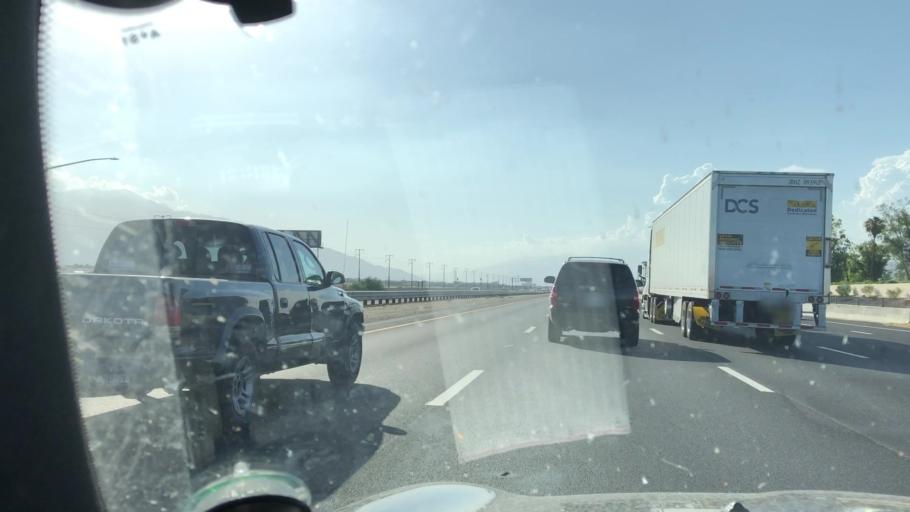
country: US
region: California
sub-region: Riverside County
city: Thousand Palms
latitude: 33.7879
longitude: -116.3575
